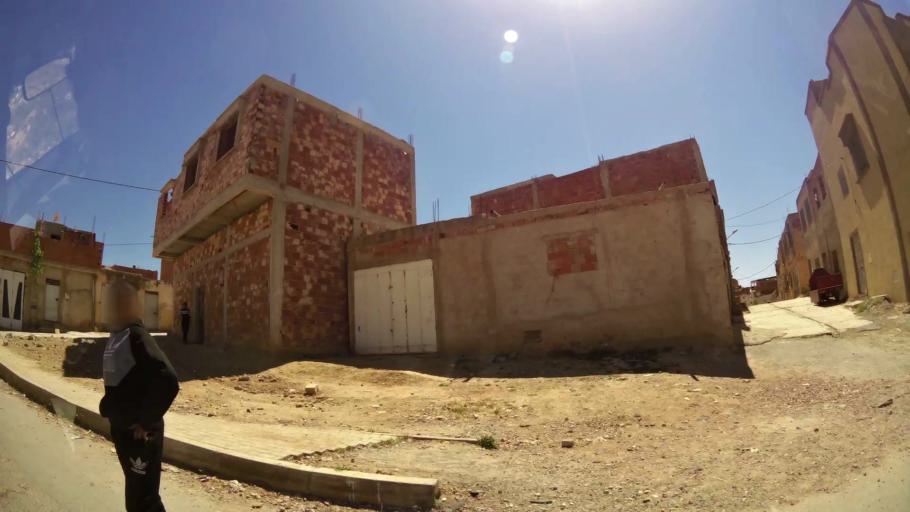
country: MA
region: Oriental
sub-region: Oujda-Angad
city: Oujda
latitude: 34.6550
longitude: -1.8651
